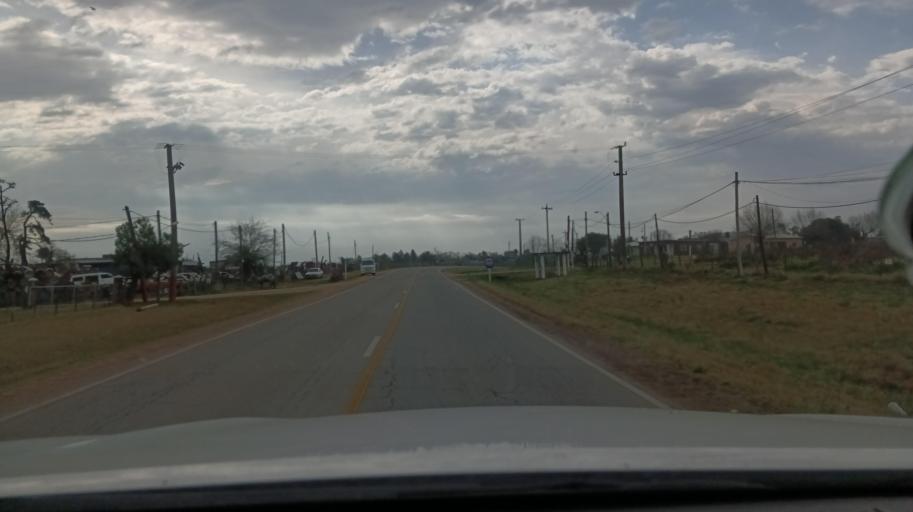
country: UY
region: Canelones
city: Toledo
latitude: -34.7175
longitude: -56.1134
